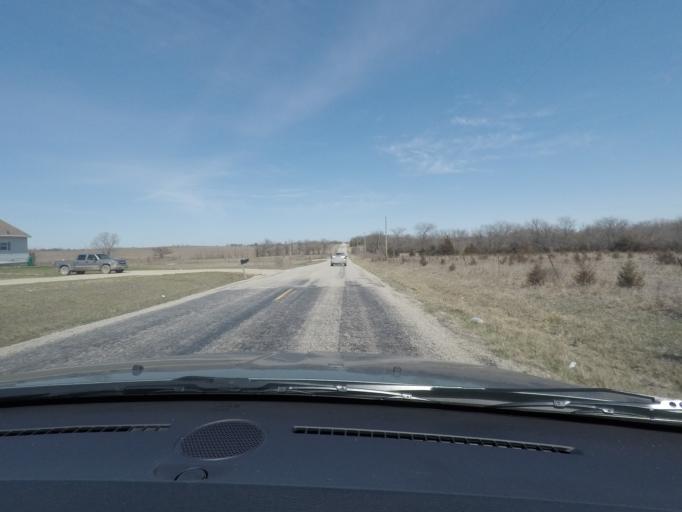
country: US
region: Kansas
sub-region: Lyon County
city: Emporia
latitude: 38.5634
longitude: -96.1699
